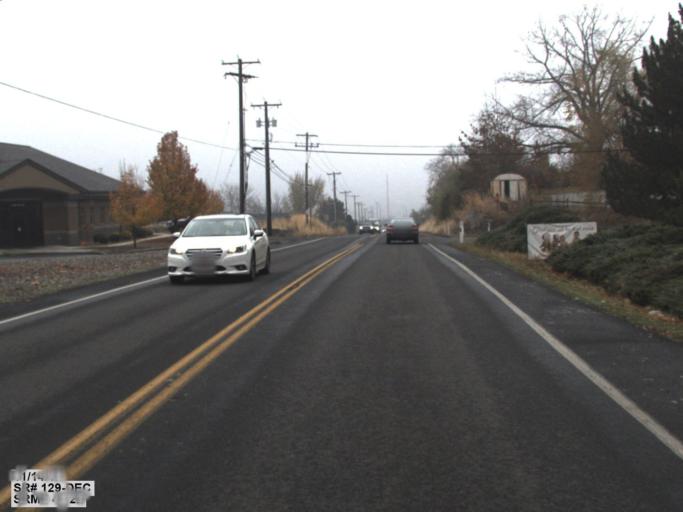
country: US
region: Washington
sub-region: Asotin County
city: Clarkston
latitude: 46.4028
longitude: -117.0443
